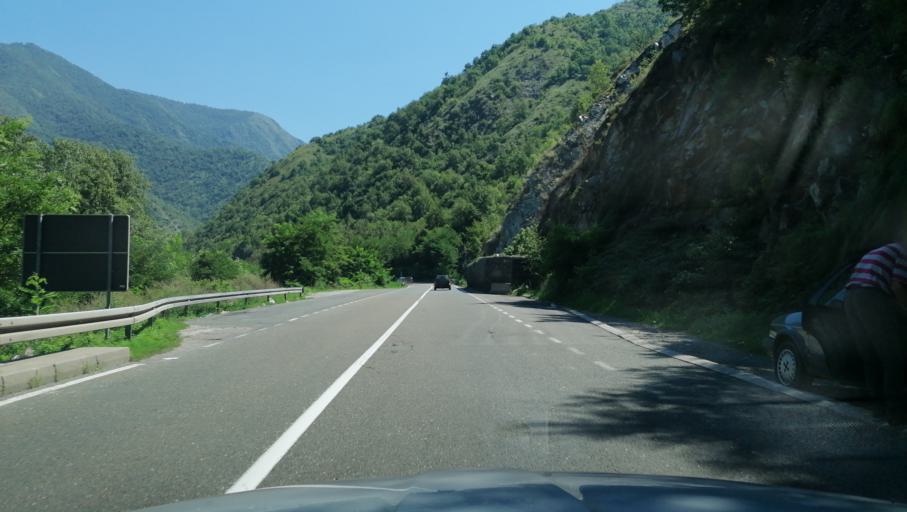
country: RS
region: Central Serbia
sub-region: Raski Okrug
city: Kraljevo
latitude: 43.5962
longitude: 20.5591
